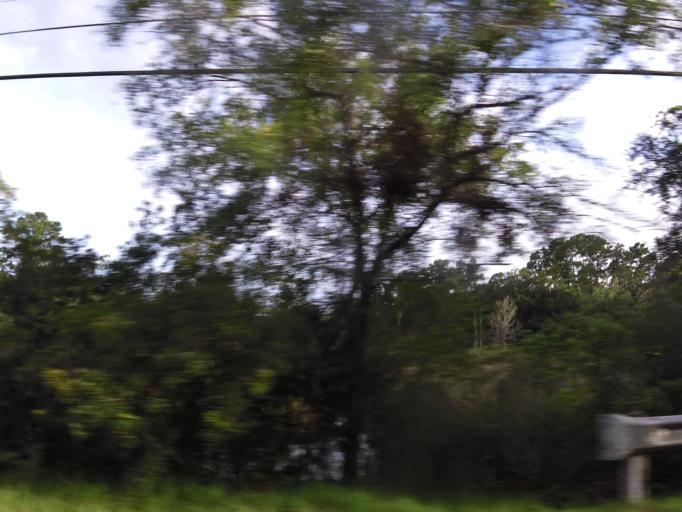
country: US
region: Florida
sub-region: Duval County
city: Jacksonville
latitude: 30.4160
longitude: -81.7339
